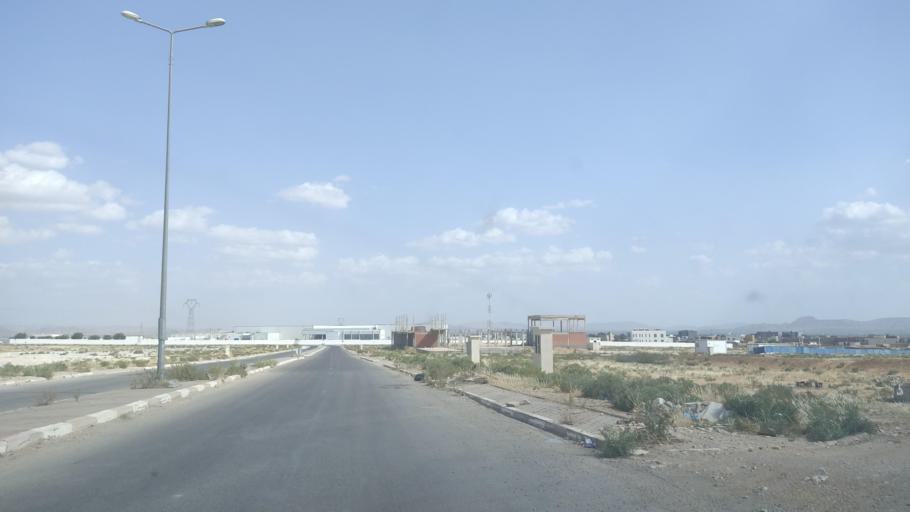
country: TN
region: Sidi Bu Zayd
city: Sidi Bouzid
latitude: 35.1075
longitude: 9.5437
